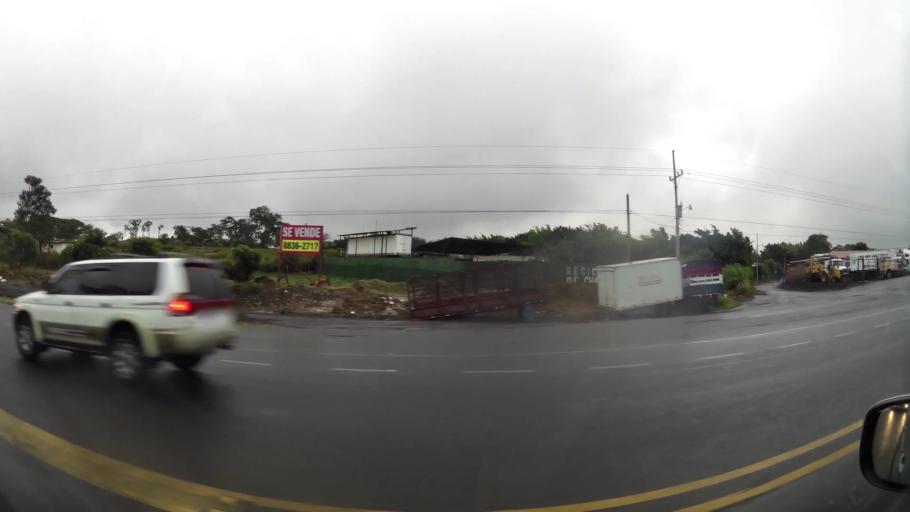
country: CR
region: Alajuela
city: Alajuela
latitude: 9.9936
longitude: -84.2469
